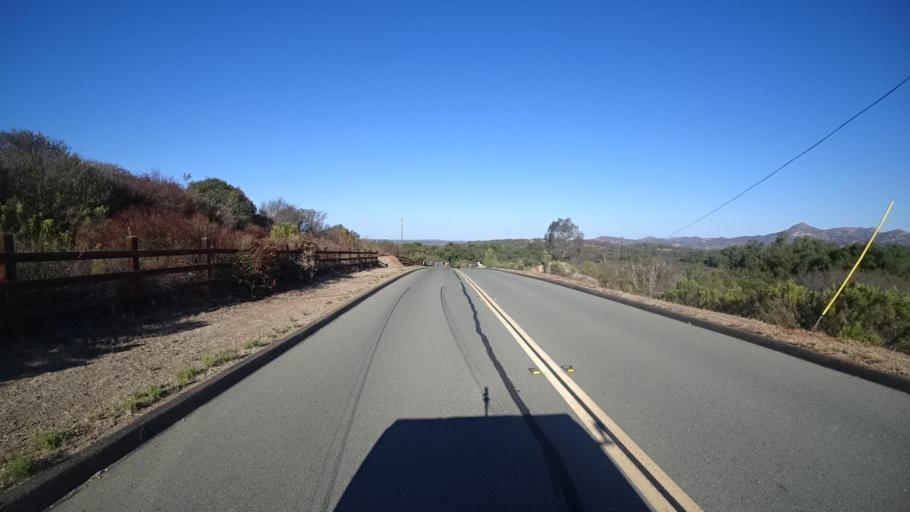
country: US
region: California
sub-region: San Diego County
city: Eucalyptus Hills
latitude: 32.9060
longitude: -116.9112
